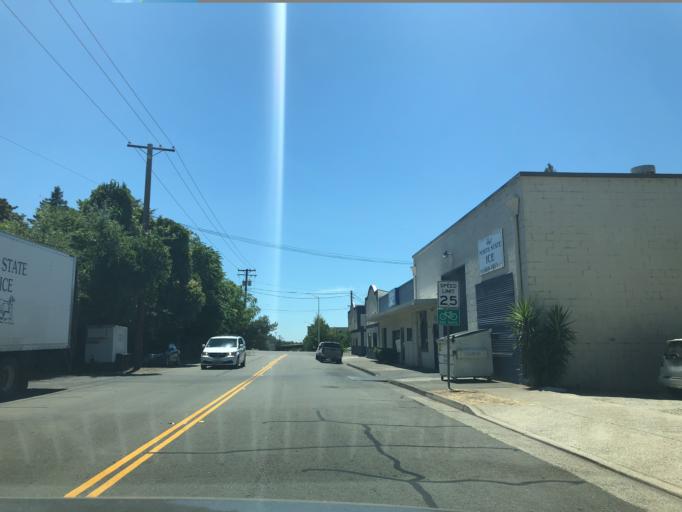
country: US
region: California
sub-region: Shasta County
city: Redding
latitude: 40.5897
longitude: -122.3877
